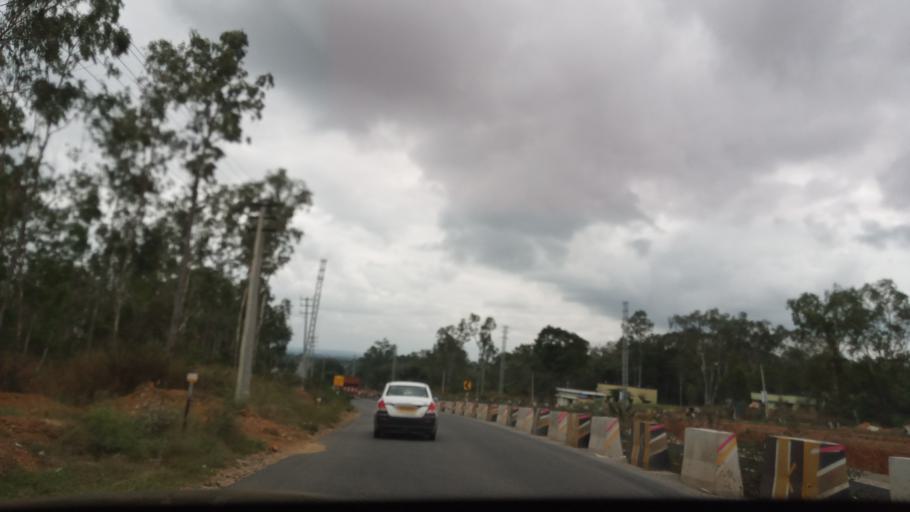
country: IN
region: Karnataka
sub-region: Mandya
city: Shrirangapattana
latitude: 12.4535
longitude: 76.7403
